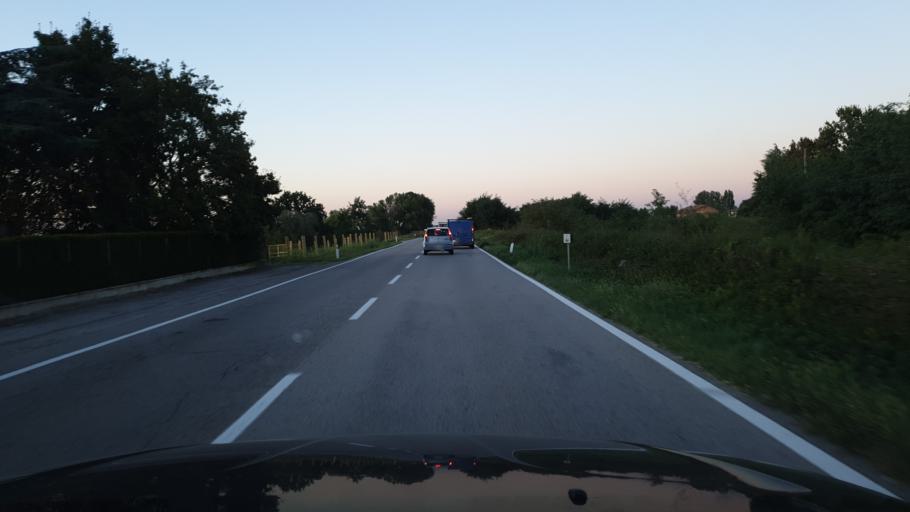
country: IT
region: Emilia-Romagna
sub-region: Provincia di Bologna
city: Ca De Fabbri
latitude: 44.6070
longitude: 11.4444
